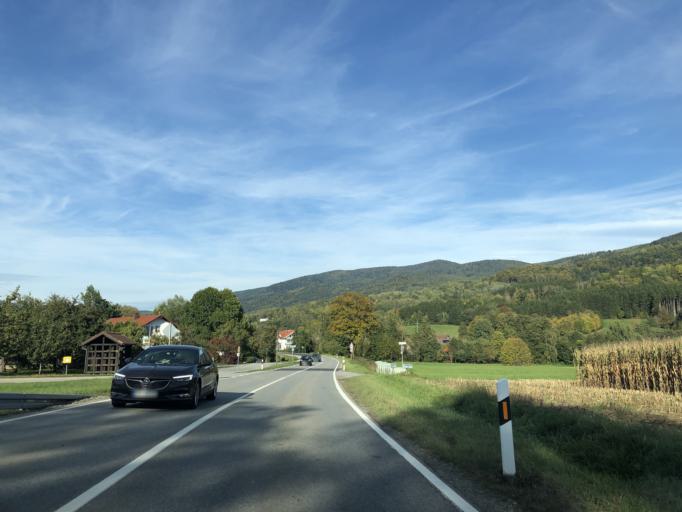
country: DE
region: Bavaria
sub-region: Lower Bavaria
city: Grafling
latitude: 48.8721
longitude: 12.9596
